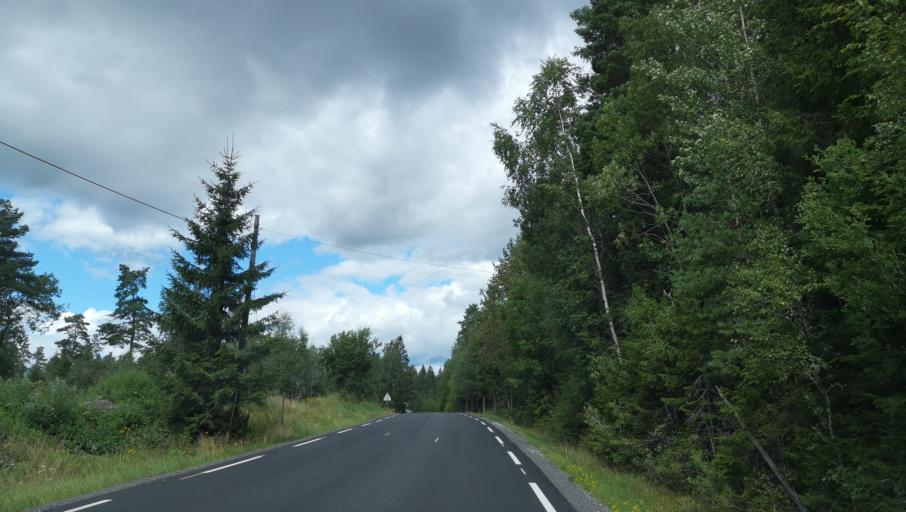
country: NO
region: Ostfold
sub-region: Hobol
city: Elvestad
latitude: 59.6835
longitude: 10.9361
